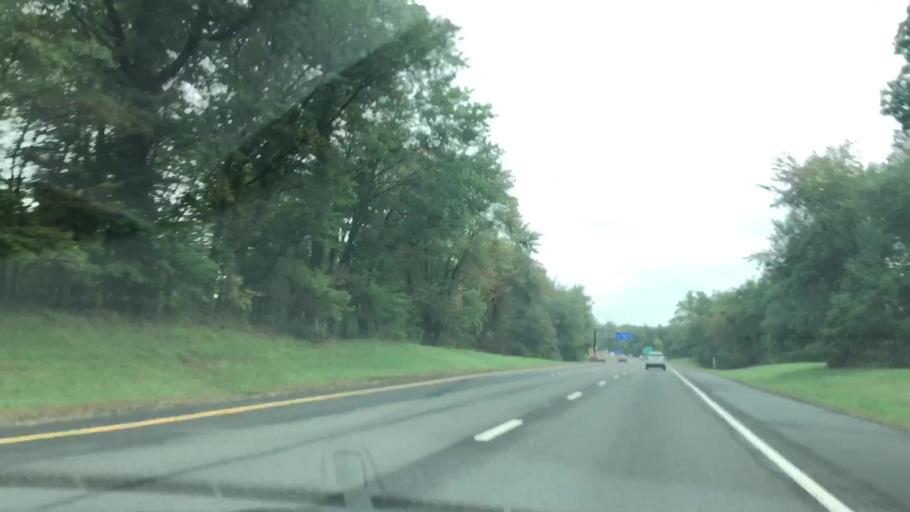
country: US
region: New Jersey
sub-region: Bergen County
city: Woodcliff Lake
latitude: 41.0426
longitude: -74.0694
